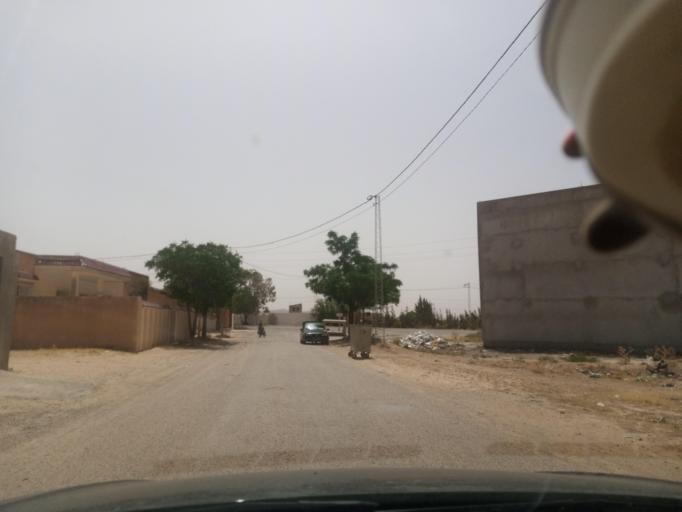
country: TN
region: Al Qasrayn
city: Kasserine
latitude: 35.2116
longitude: 8.8998
